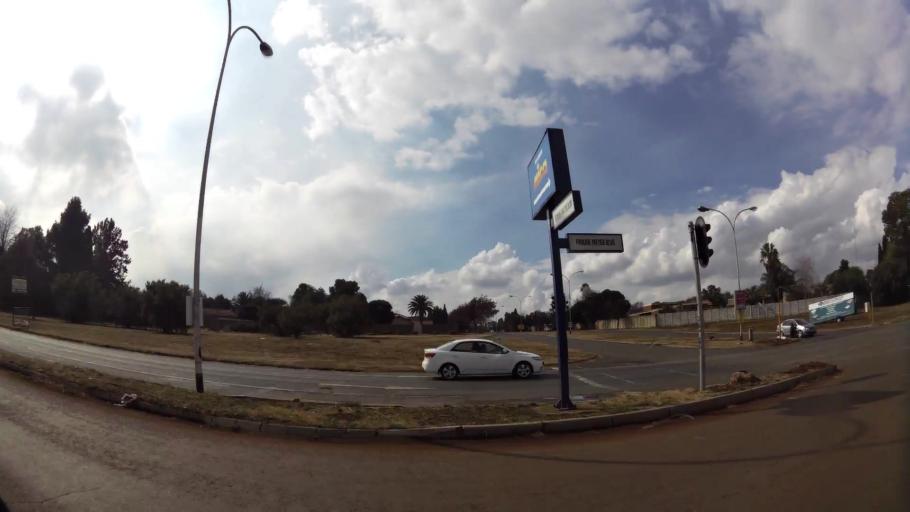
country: ZA
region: Gauteng
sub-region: Sedibeng District Municipality
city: Vanderbijlpark
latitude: -26.7348
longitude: 27.8420
